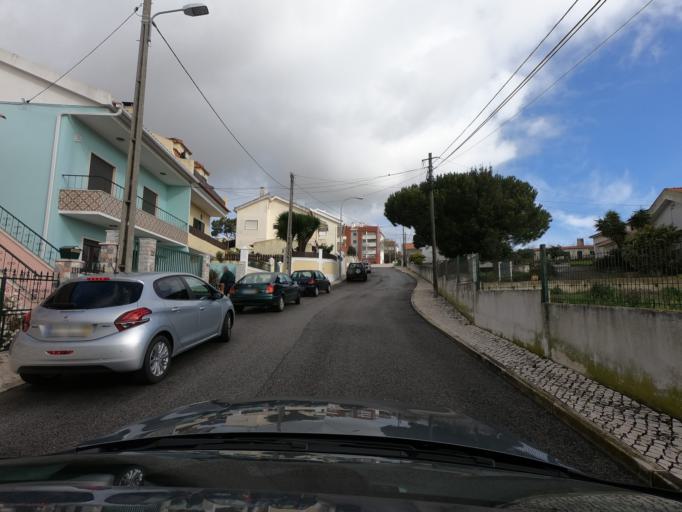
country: PT
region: Lisbon
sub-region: Cascais
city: Sao Domingos de Rana
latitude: 38.7101
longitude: -9.3249
